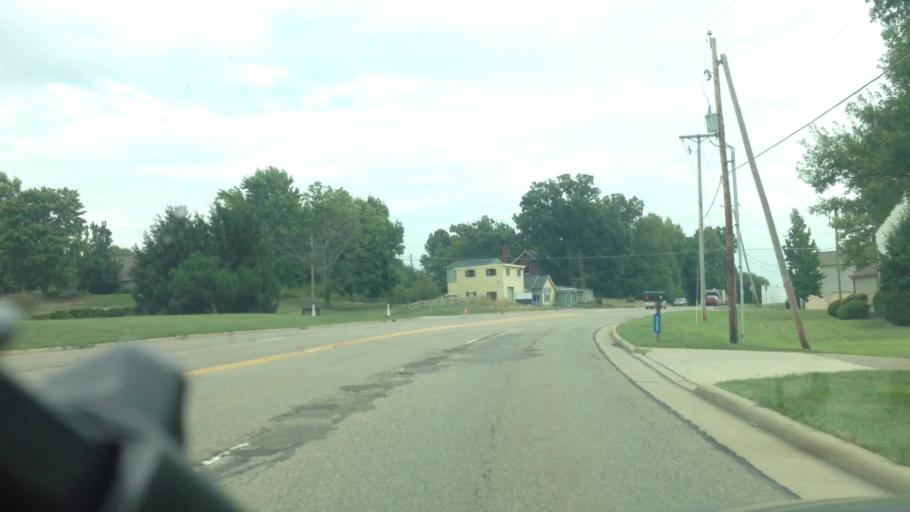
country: US
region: Ohio
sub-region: Stark County
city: Perry Heights
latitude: 40.8341
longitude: -81.4738
